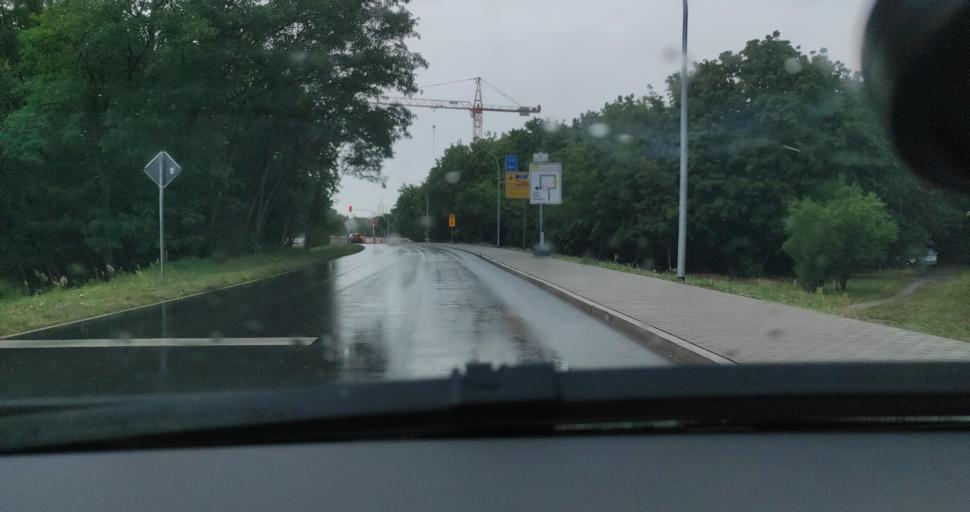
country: DE
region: Brandenburg
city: Forst
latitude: 51.7267
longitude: 14.6331
